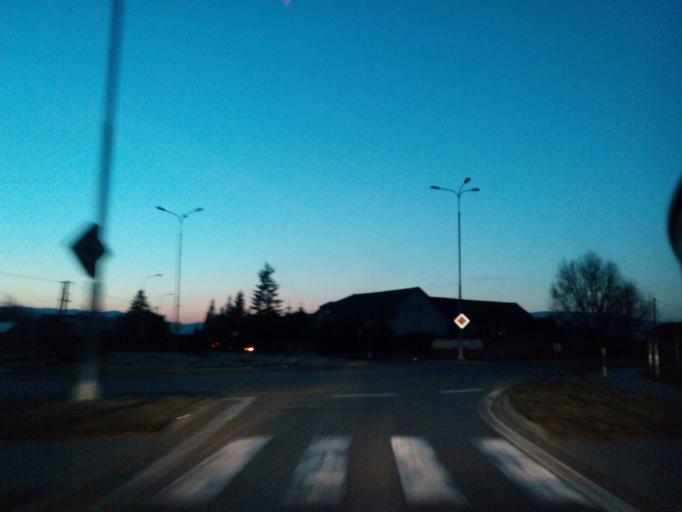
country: SK
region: Kosicky
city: Secovce
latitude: 48.6994
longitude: 21.7075
